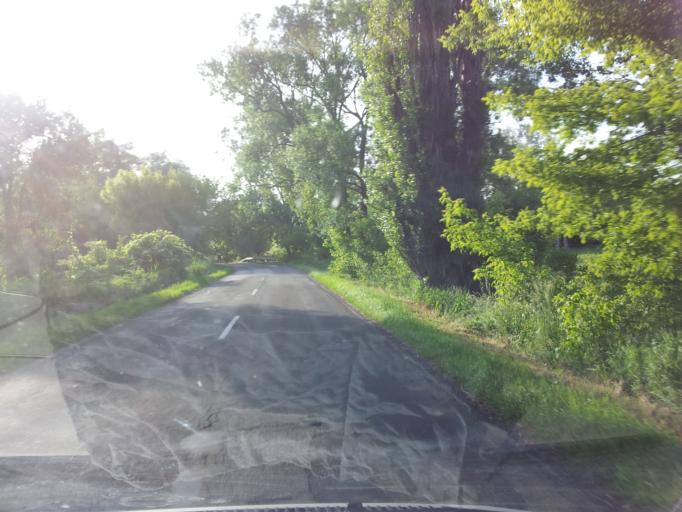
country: HU
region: Komarom-Esztergom
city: Kesztolc
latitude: 47.7558
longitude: 18.7760
